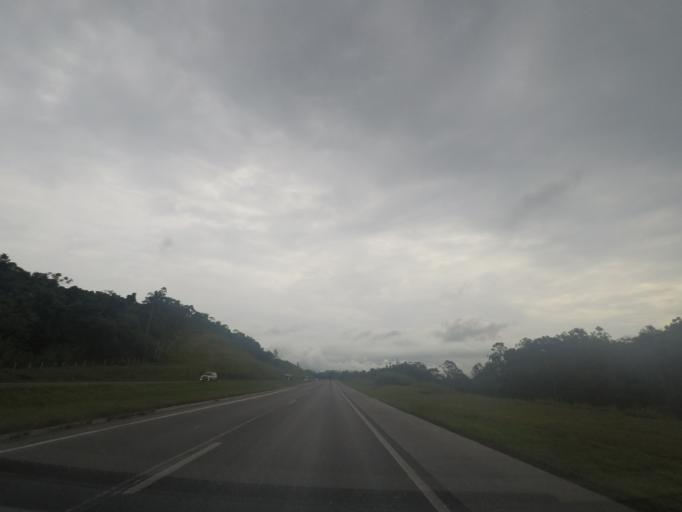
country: BR
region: Sao Paulo
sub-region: Cajati
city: Cajati
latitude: -24.7247
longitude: -48.0878
